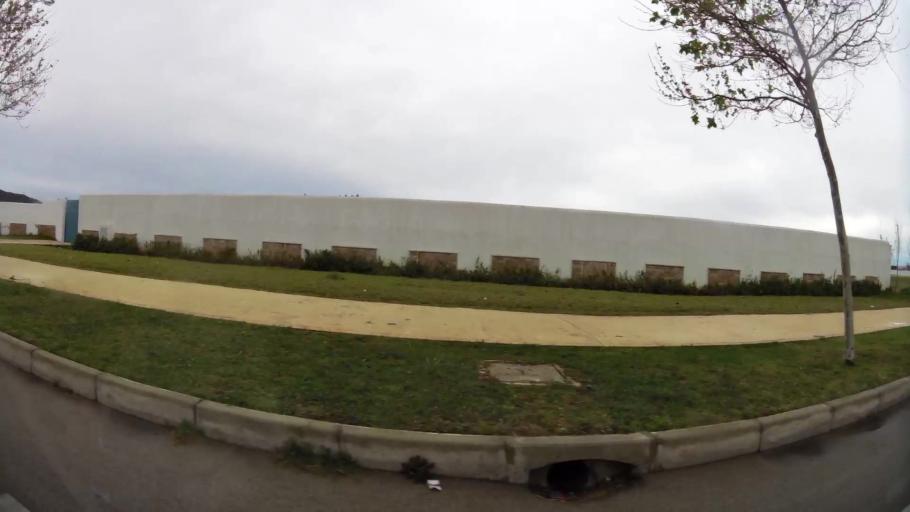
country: MA
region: Tanger-Tetouan
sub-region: Tetouan
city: Martil
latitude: 35.6399
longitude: -5.2914
